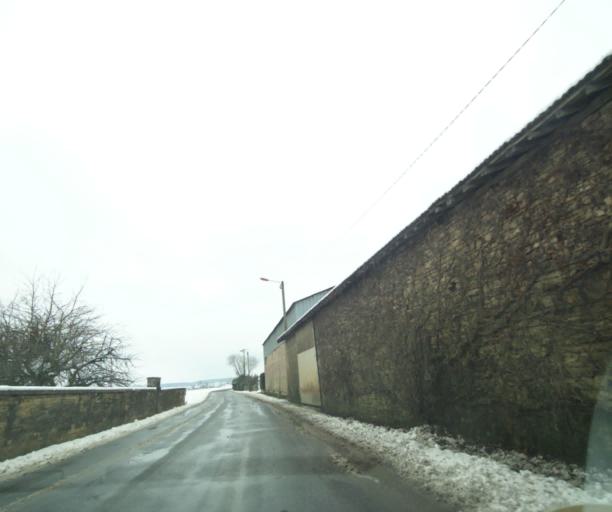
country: FR
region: Champagne-Ardenne
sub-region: Departement de la Haute-Marne
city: Montier-en-Der
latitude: 48.4191
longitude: 4.8211
